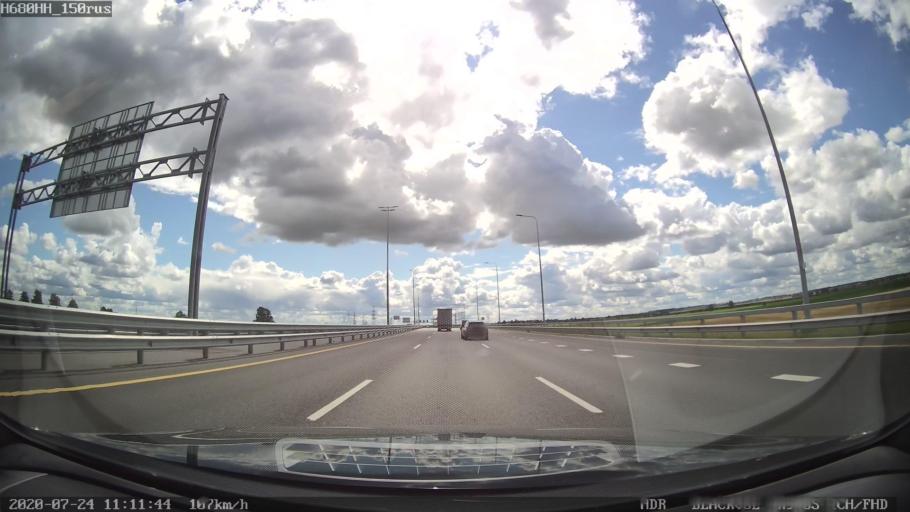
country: RU
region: Leningrad
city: Fedorovskoye
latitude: 59.7185
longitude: 30.5206
